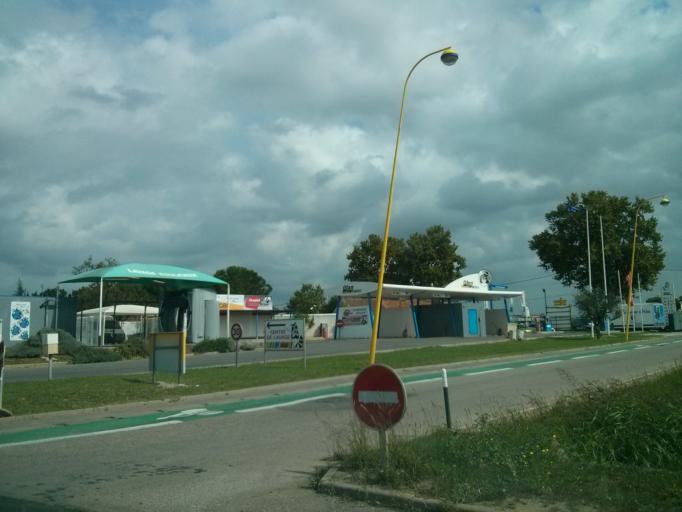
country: FR
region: Languedoc-Roussillon
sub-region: Departement de l'Herault
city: Lunel
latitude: 43.6842
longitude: 4.1494
